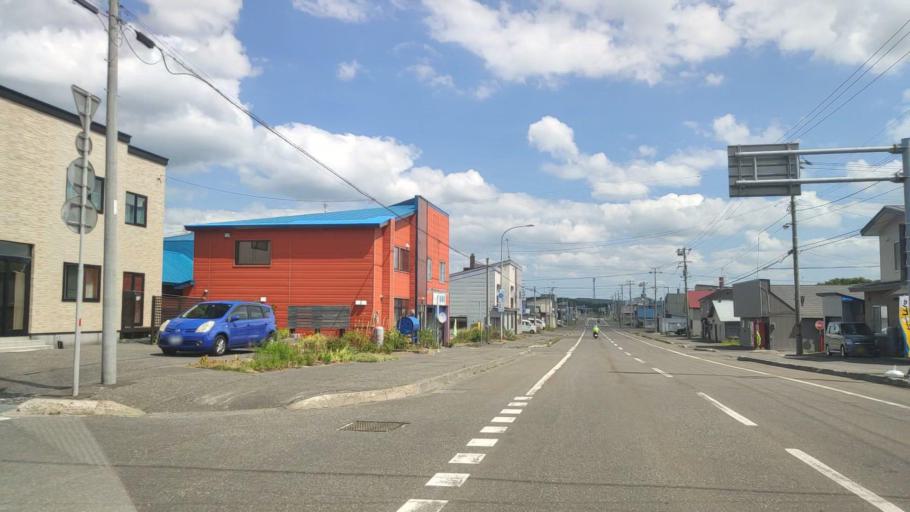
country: JP
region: Hokkaido
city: Makubetsu
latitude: 44.8830
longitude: 141.7436
